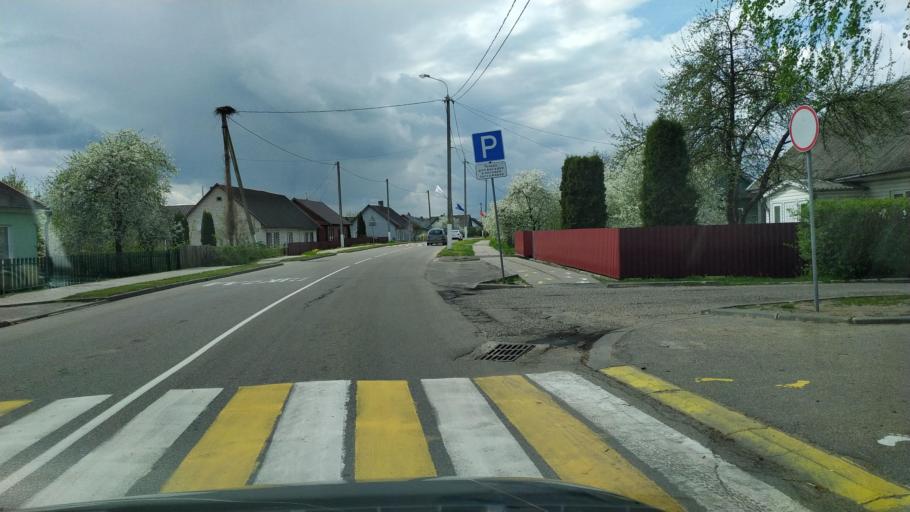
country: BY
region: Brest
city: Pruzhany
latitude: 52.5555
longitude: 24.4462
